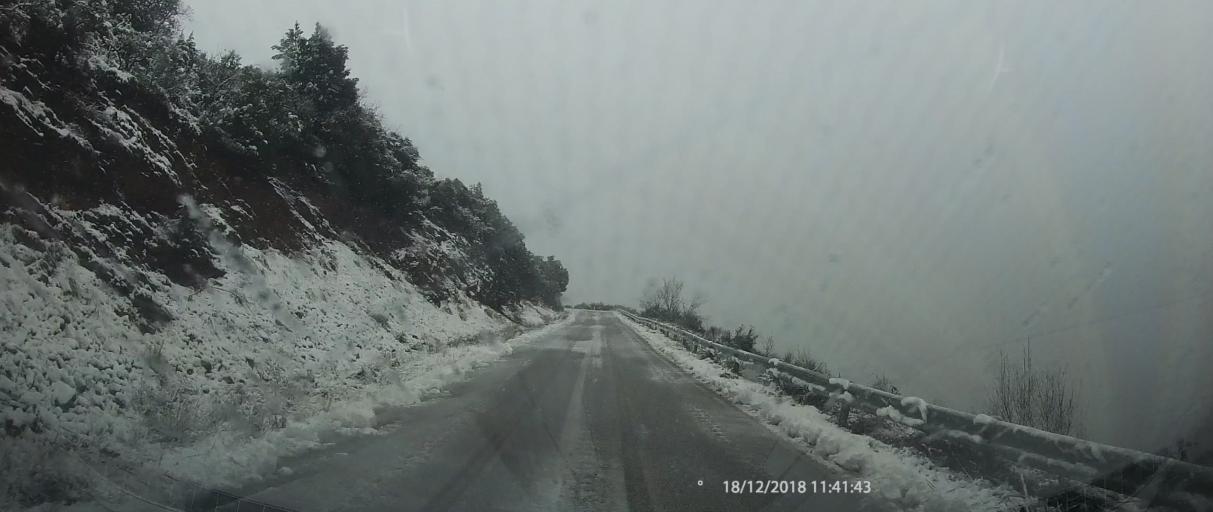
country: GR
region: Central Macedonia
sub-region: Nomos Pierias
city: Litochoro
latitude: 40.1084
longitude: 22.4737
